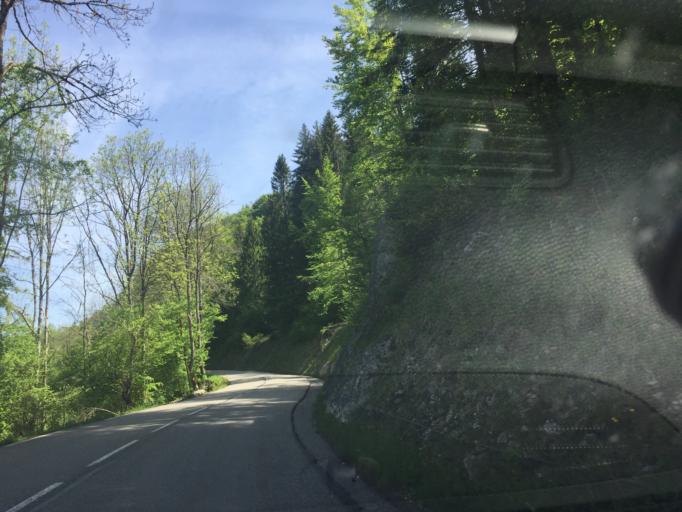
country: FR
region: Rhone-Alpes
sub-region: Departement de l'Isere
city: Barraux
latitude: 45.4402
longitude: 5.8788
